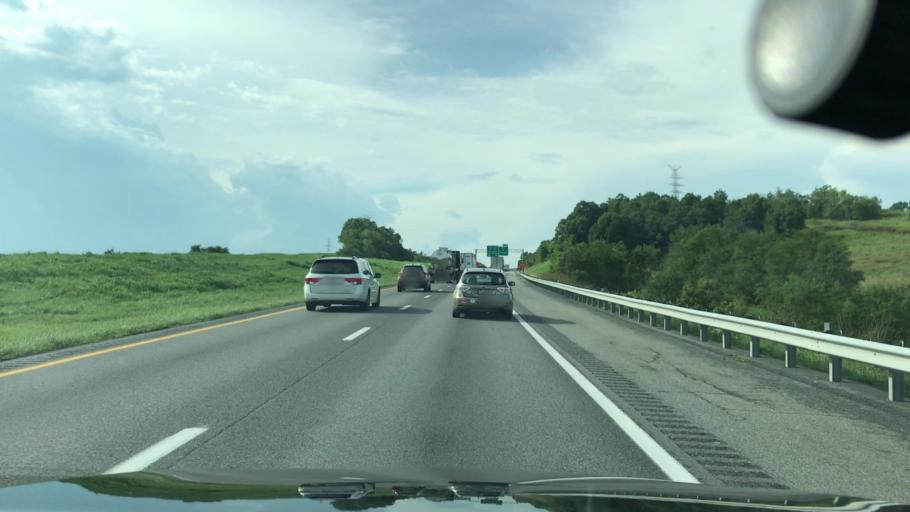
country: US
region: Virginia
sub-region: Wythe County
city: Wytheville
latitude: 36.9343
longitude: -80.9130
